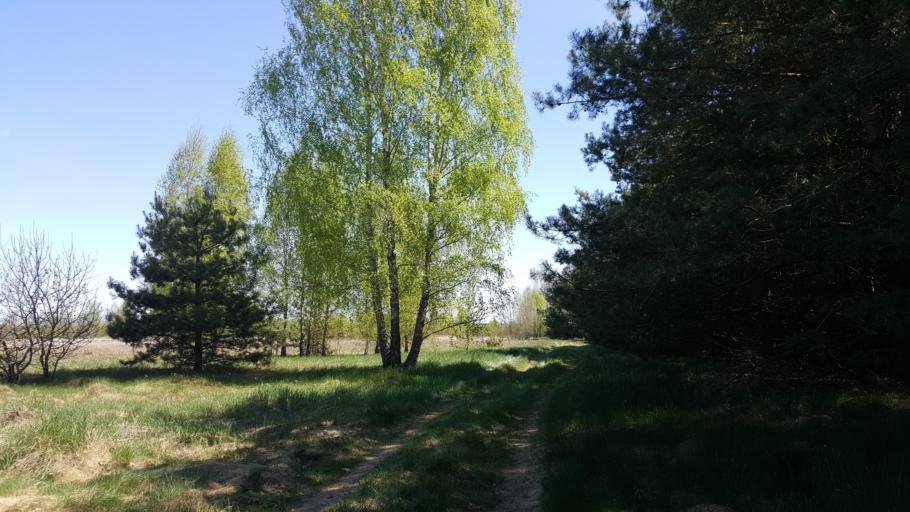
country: BY
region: Brest
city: Kamyanyets
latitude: 52.4272
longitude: 23.8518
